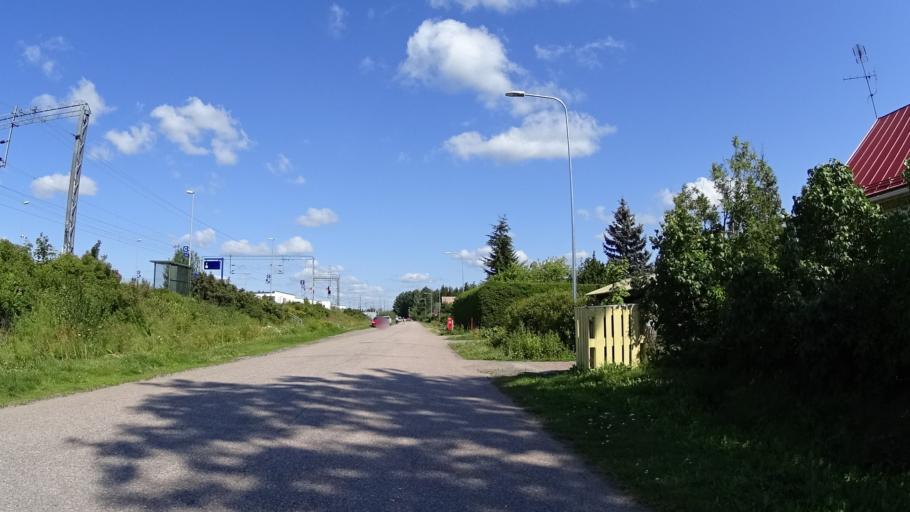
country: FI
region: Uusimaa
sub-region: Helsinki
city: Jaervenpaeae
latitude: 60.4570
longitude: 25.1021
